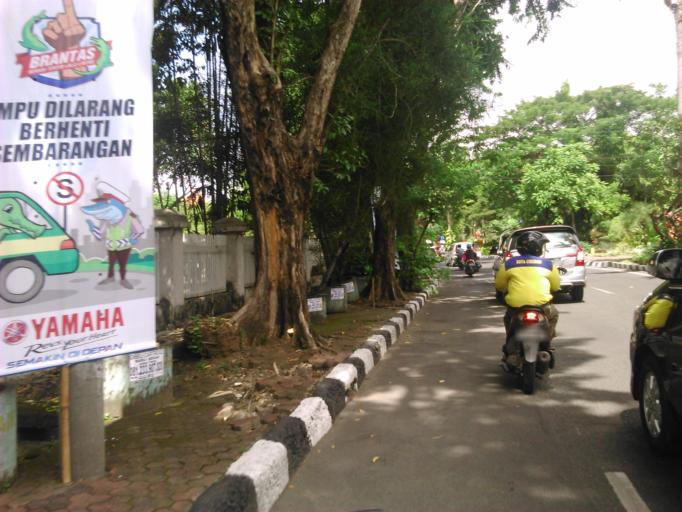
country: ID
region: East Java
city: Gubengairlangga
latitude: -7.2830
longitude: 112.7371
